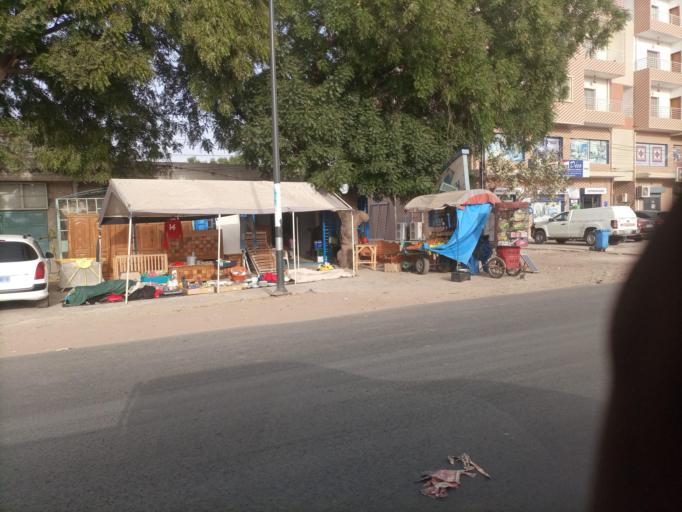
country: SN
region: Thies
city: Warang
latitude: 14.4380
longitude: -16.9778
